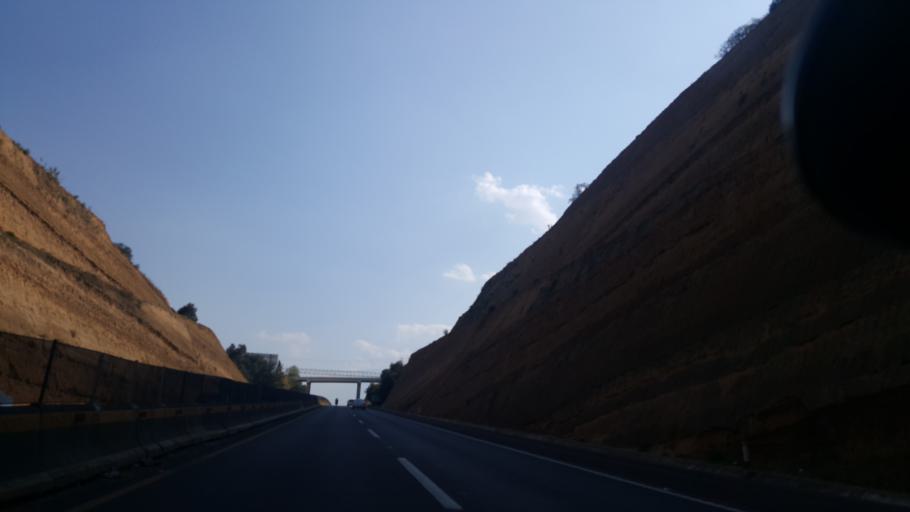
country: MX
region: Mexico
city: Ciudad Lopez Mateos
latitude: 19.5765
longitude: -99.2698
